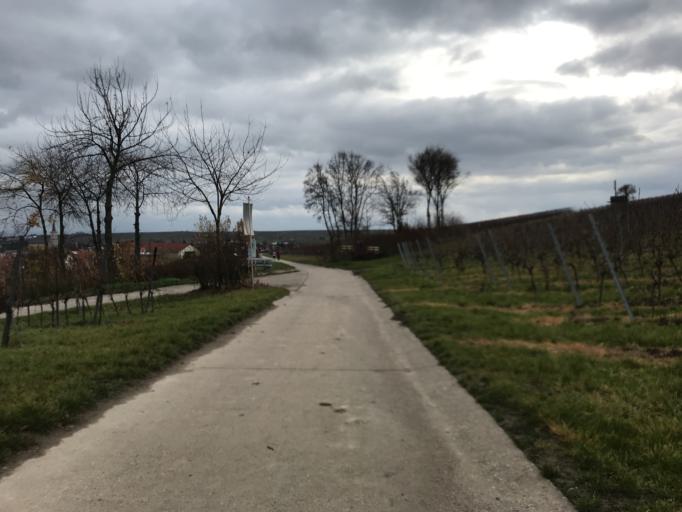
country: DE
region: Rheinland-Pfalz
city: Bodenheim
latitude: 49.9330
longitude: 8.2963
